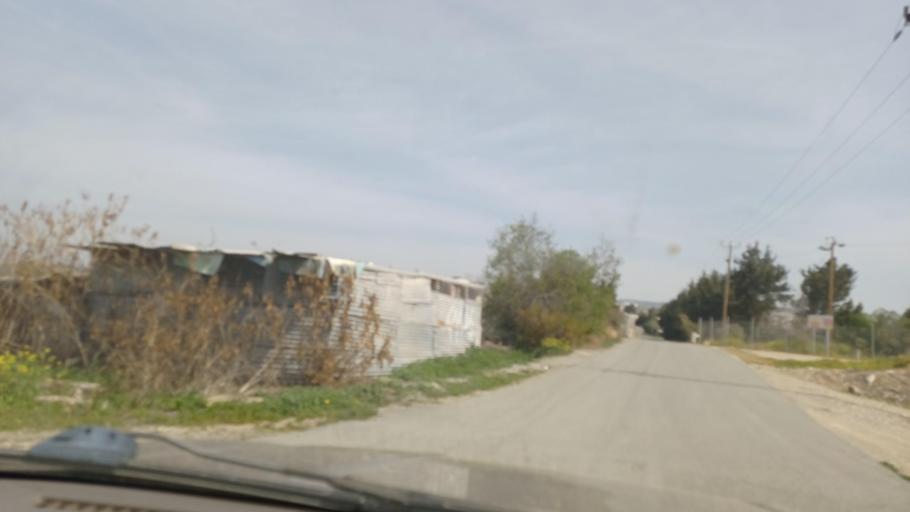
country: CY
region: Pafos
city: Paphos
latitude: 34.7465
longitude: 32.4622
